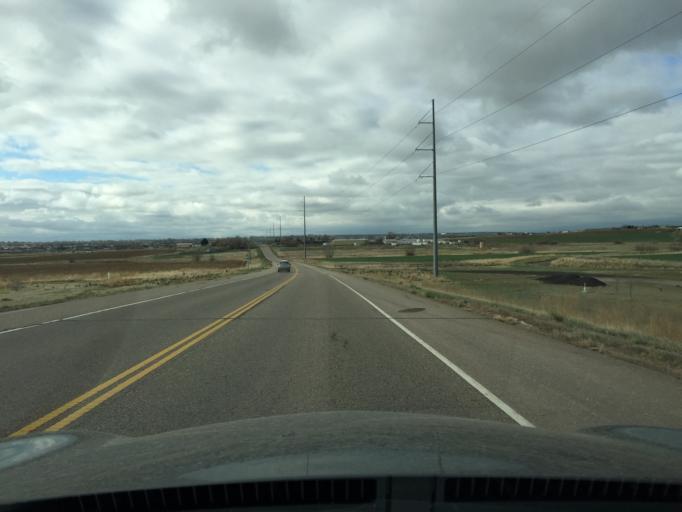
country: US
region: Colorado
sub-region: Adams County
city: Northglenn
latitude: 39.9785
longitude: -104.9782
